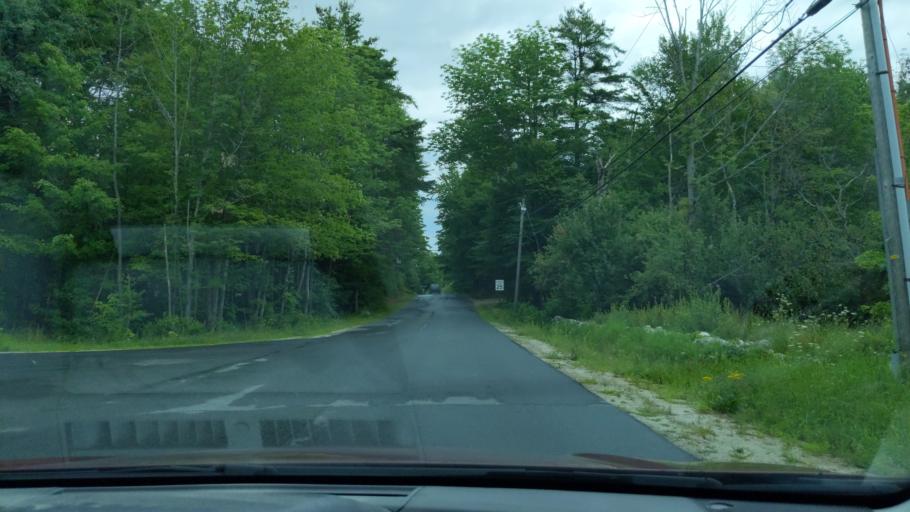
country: US
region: New Hampshire
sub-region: Merrimack County
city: New London
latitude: 43.4168
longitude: -72.0165
